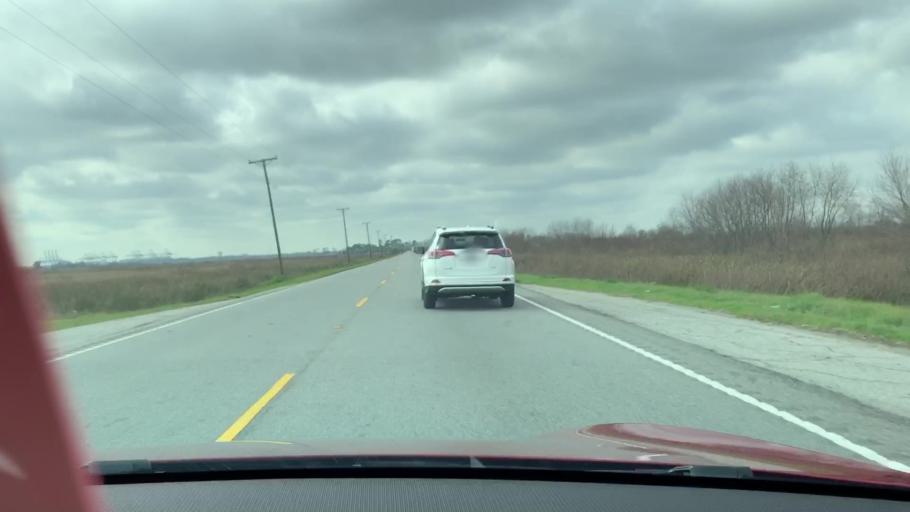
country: US
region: Georgia
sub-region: Chatham County
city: Port Wentworth
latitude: 32.1713
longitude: -81.1017
